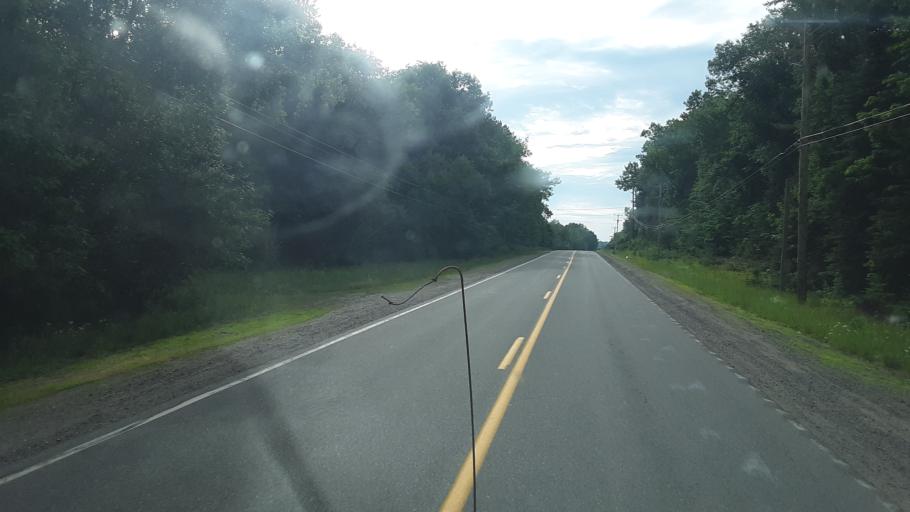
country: US
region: Maine
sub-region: Penobscot County
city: Medway
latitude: 45.5983
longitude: -68.5073
